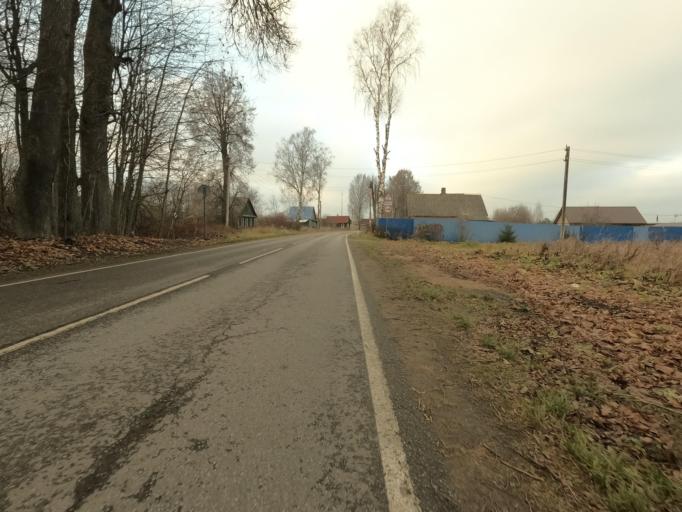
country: RU
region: Leningrad
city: Mga
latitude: 59.7729
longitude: 31.0240
